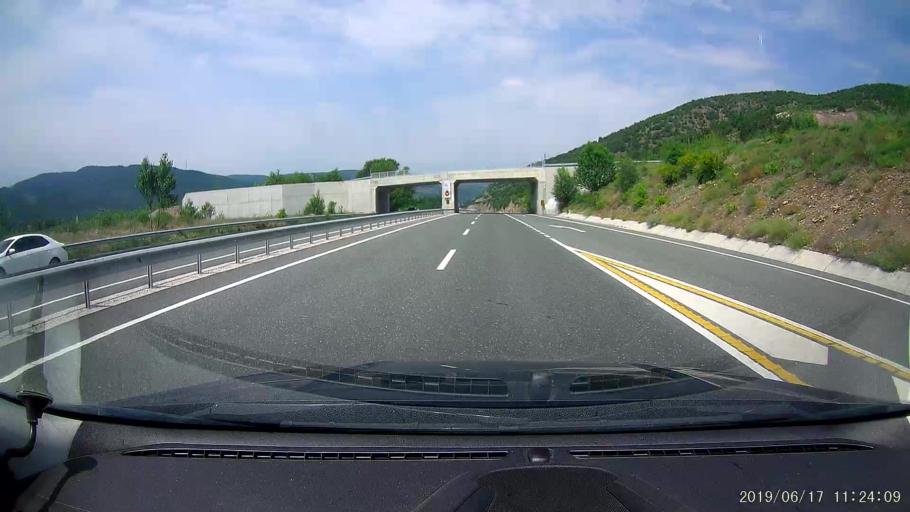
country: TR
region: Cankiri
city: Ilgaz
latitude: 40.8843
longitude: 33.7125
